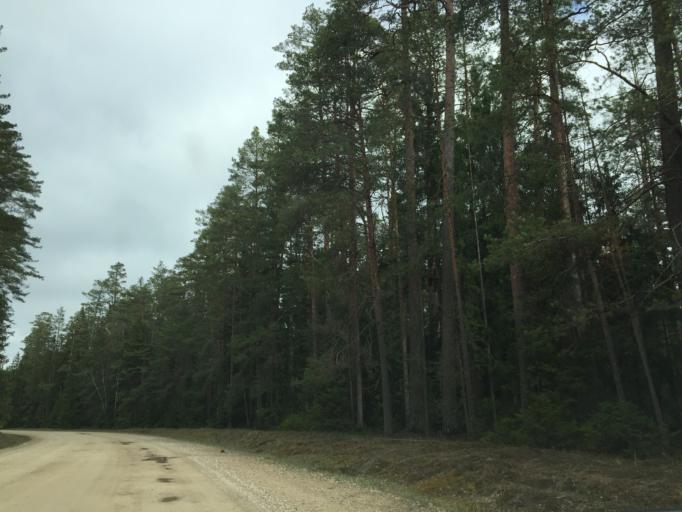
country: EE
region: Valgamaa
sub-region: Valga linn
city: Valga
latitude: 57.5875
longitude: 26.2204
